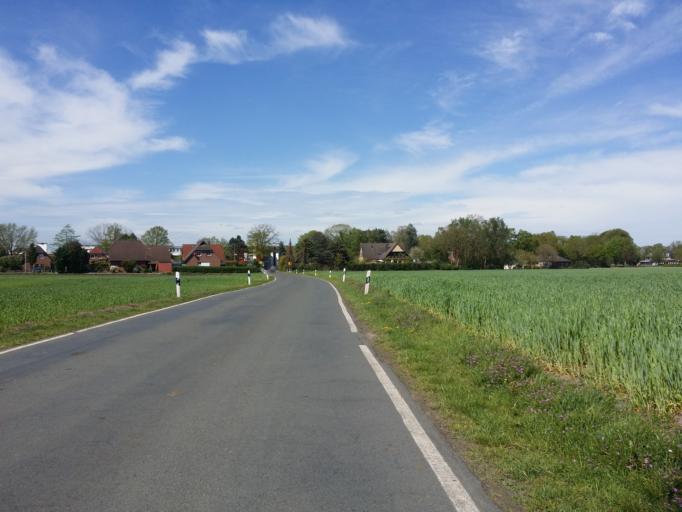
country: DE
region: Lower Saxony
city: Delmenhorst
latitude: 53.0781
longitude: 8.6489
